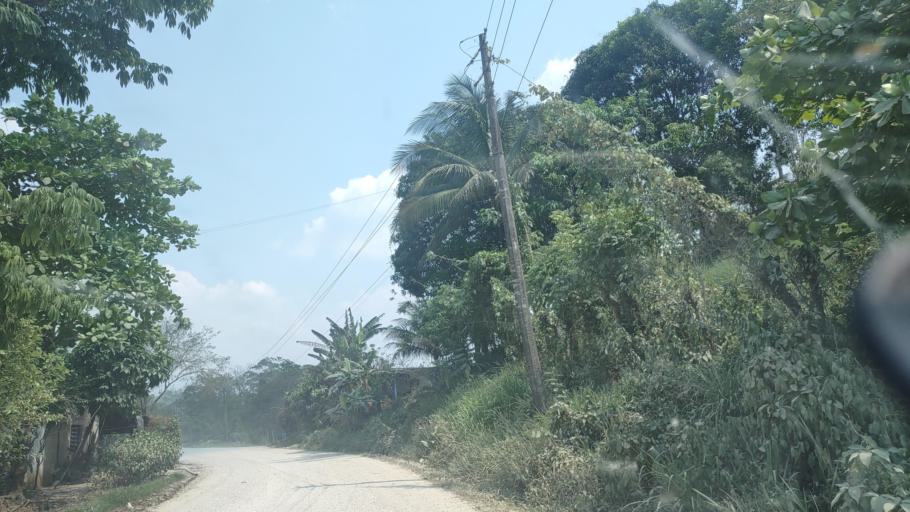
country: MX
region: Tabasco
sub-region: Huimanguillo
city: Francisco Rueda
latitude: 17.5936
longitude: -93.8976
